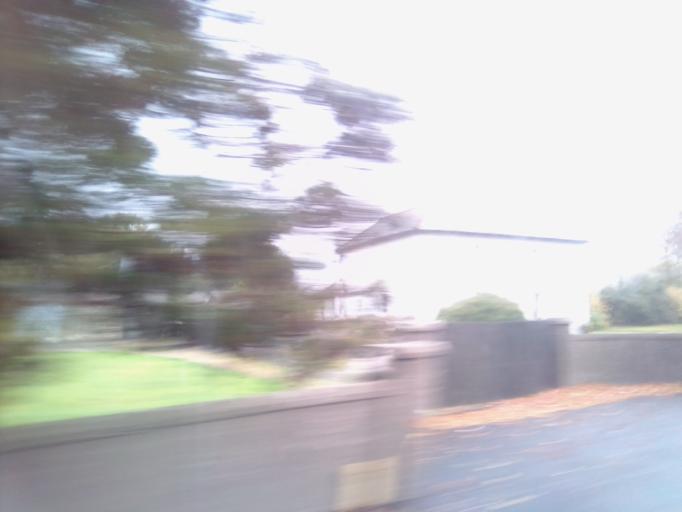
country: IE
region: Leinster
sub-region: Uibh Fhaili
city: Birr
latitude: 53.0517
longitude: -7.9044
